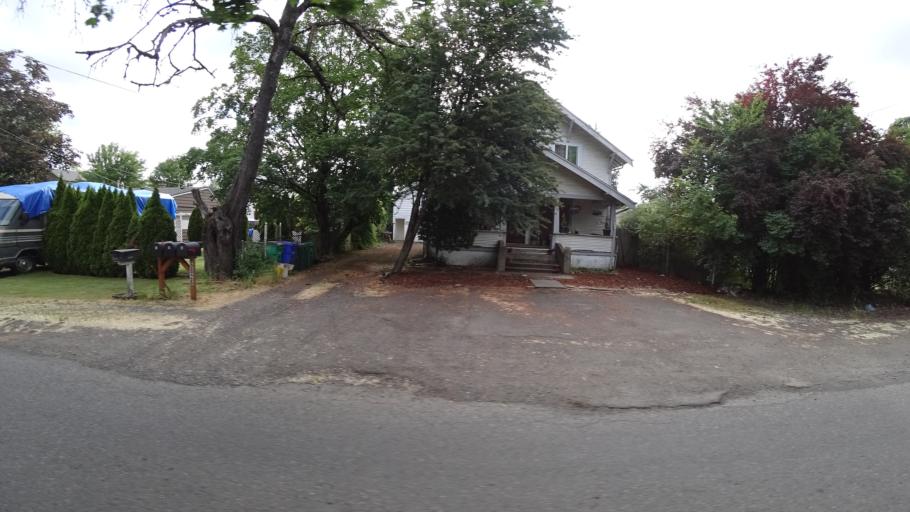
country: US
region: Oregon
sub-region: Multnomah County
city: Lents
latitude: 45.4801
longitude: -122.5574
